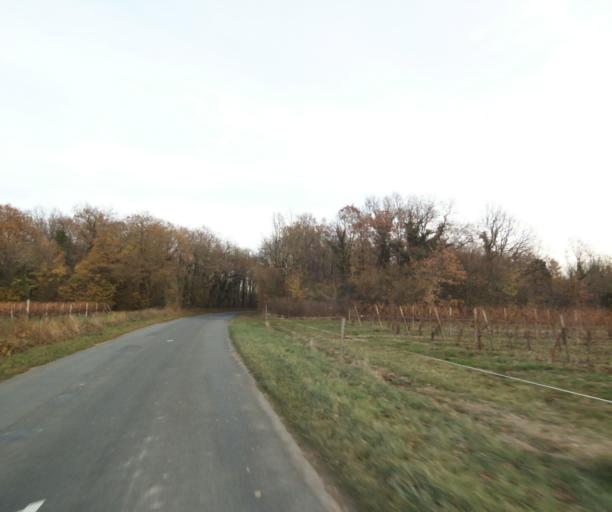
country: FR
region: Poitou-Charentes
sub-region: Departement de la Charente-Maritime
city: Fontcouverte
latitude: 45.7986
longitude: -0.5717
